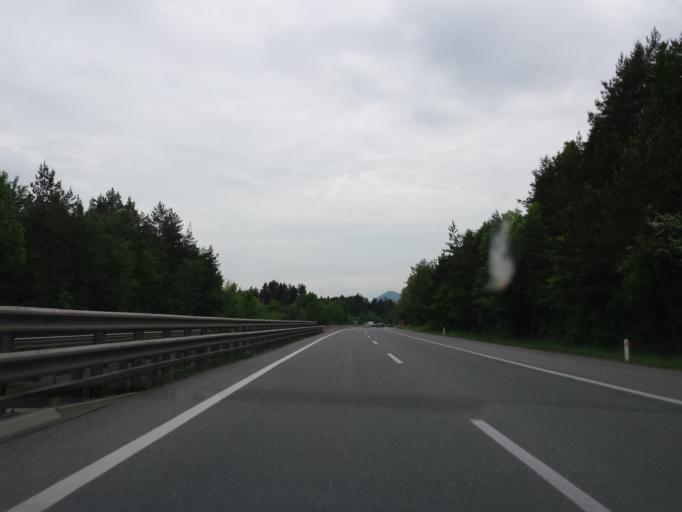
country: AT
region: Lower Austria
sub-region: Politischer Bezirk Neunkirchen
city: Seebenstein
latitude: 47.6965
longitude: 16.1301
